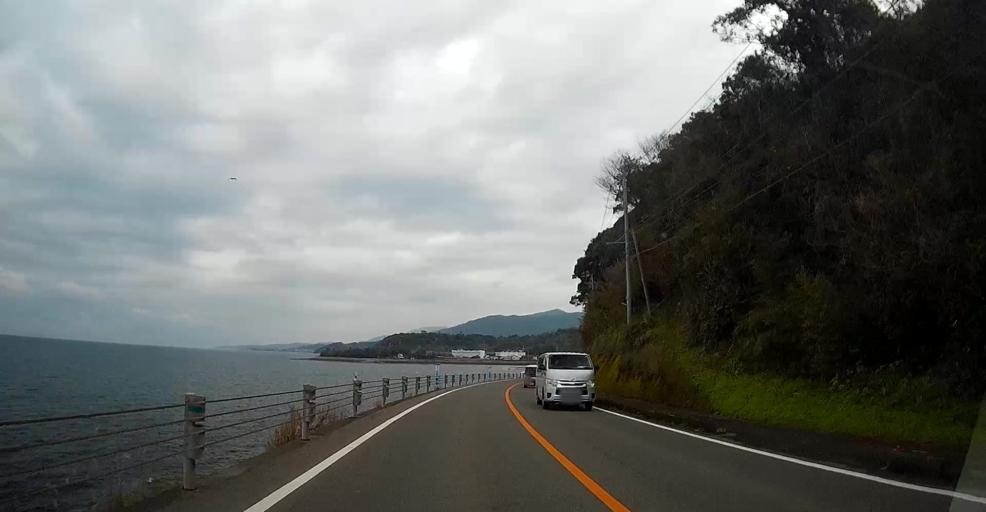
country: JP
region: Kumamoto
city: Hondo
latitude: 32.4573
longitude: 130.2175
